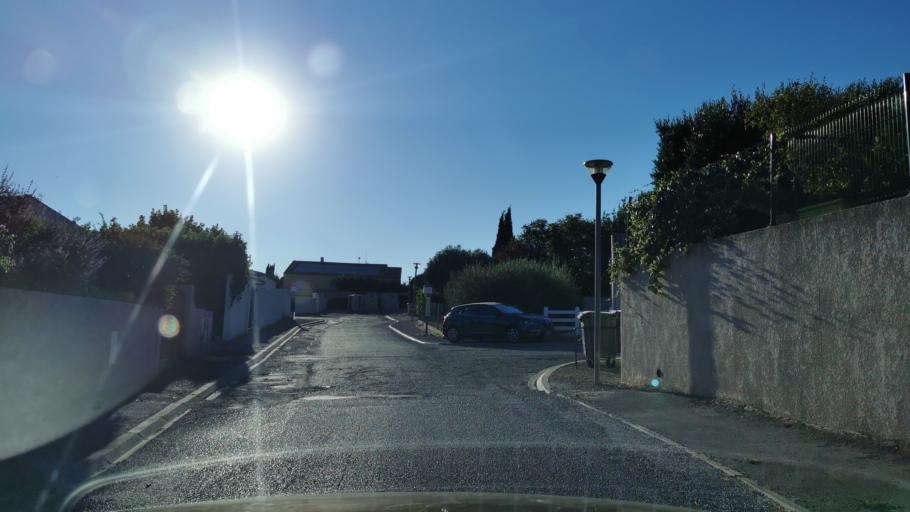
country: FR
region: Languedoc-Roussillon
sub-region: Departement de l'Aude
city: Ouveillan
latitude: 43.2870
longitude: 2.9646
